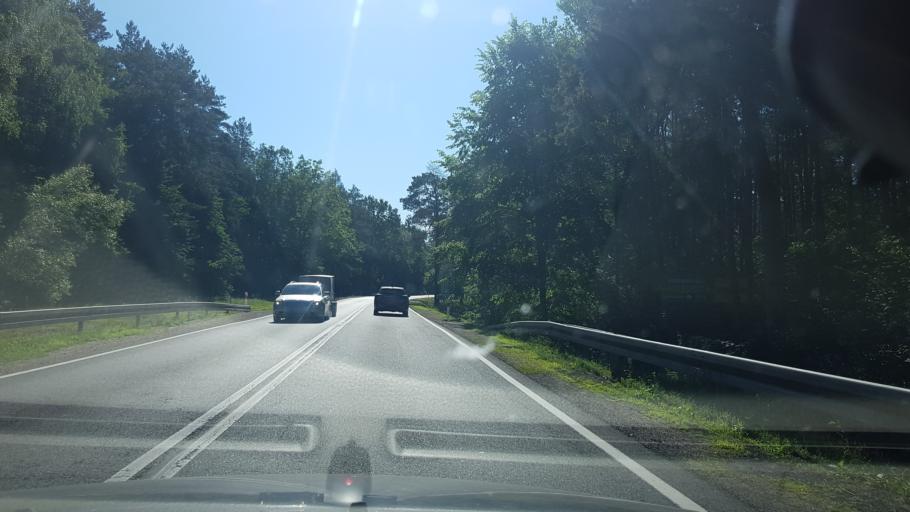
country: PL
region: Masovian Voivodeship
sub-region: Powiat wyszkowski
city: Branszczyk
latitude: 52.5547
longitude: 21.5983
